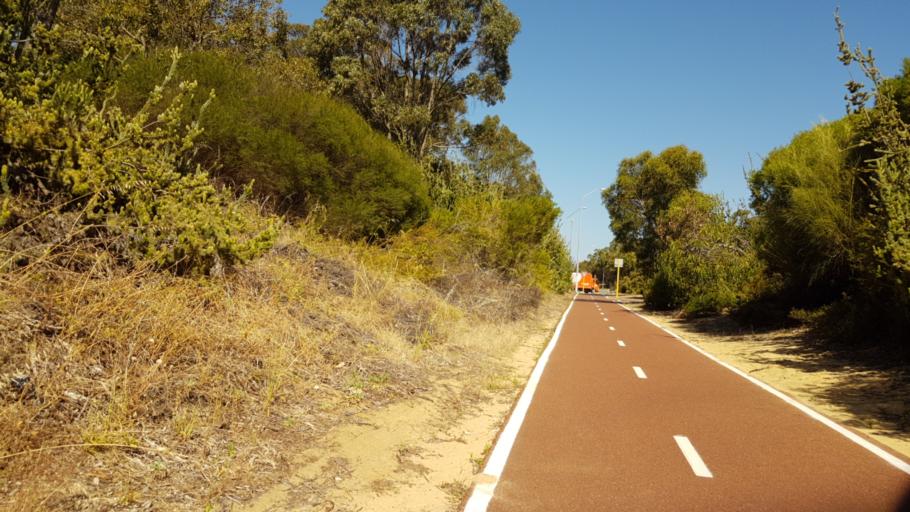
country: AU
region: Western Australia
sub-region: Stirling
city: Karrinyup
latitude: -31.8564
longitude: 115.7885
